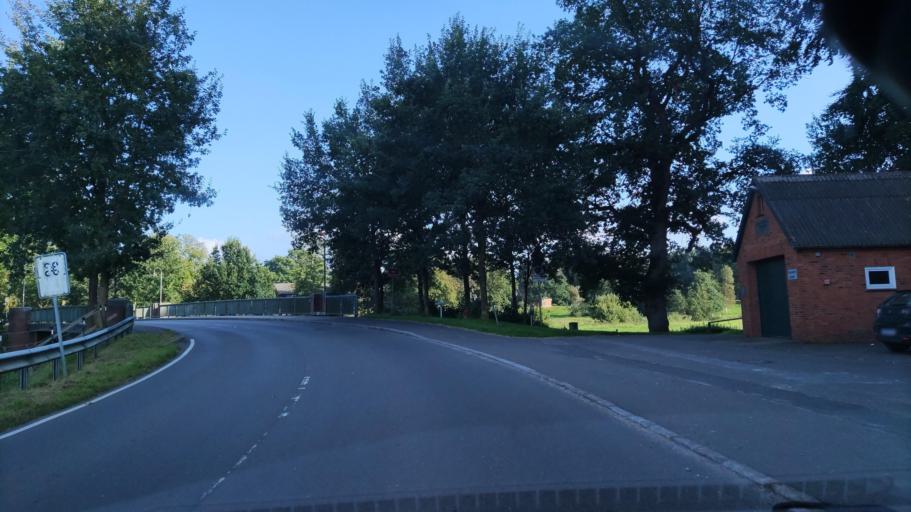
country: DE
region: Schleswig-Holstein
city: Willenscharen
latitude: 54.0103
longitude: 9.8059
